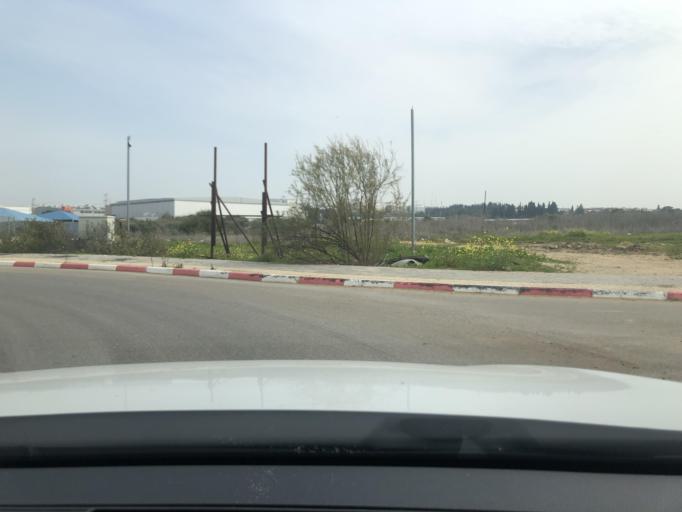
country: IL
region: Central District
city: Rosh Ha'Ayin
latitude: 32.1048
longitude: 34.9494
